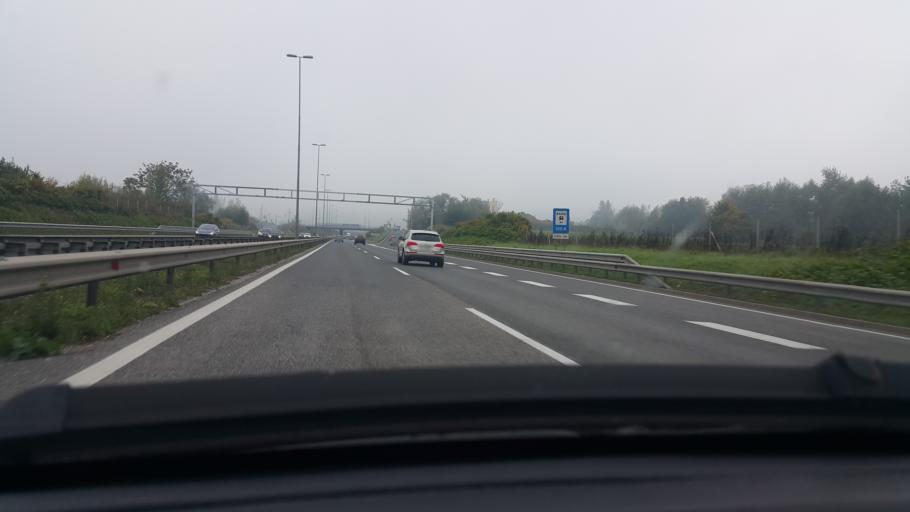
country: SI
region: Dol pri Ljubljani
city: Dol pri Ljubljani
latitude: 46.0477
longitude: 14.5756
